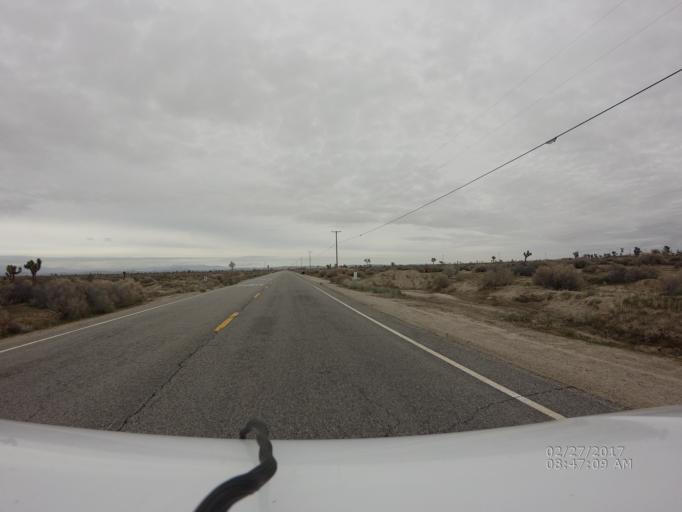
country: US
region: California
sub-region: Los Angeles County
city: Lancaster
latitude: 34.7207
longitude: -118.0771
